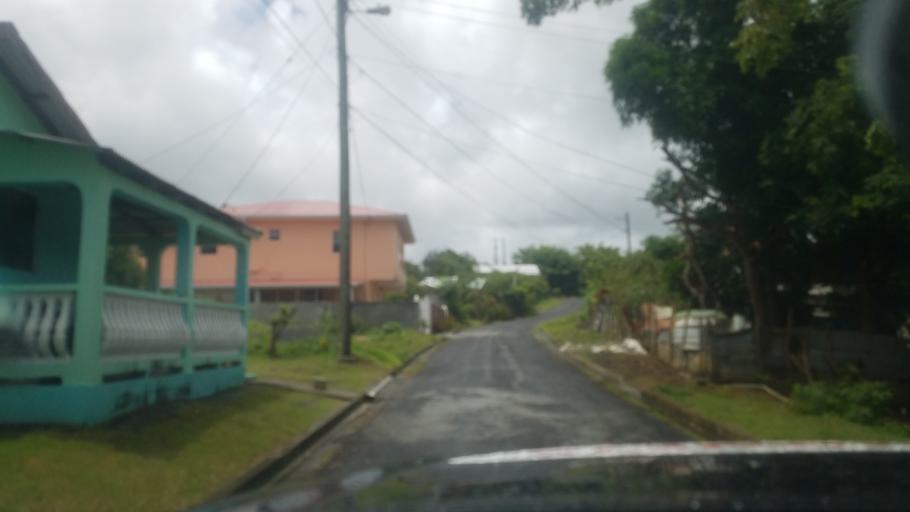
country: LC
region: Laborie Quarter
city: Laborie
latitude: 13.7517
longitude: -60.9780
